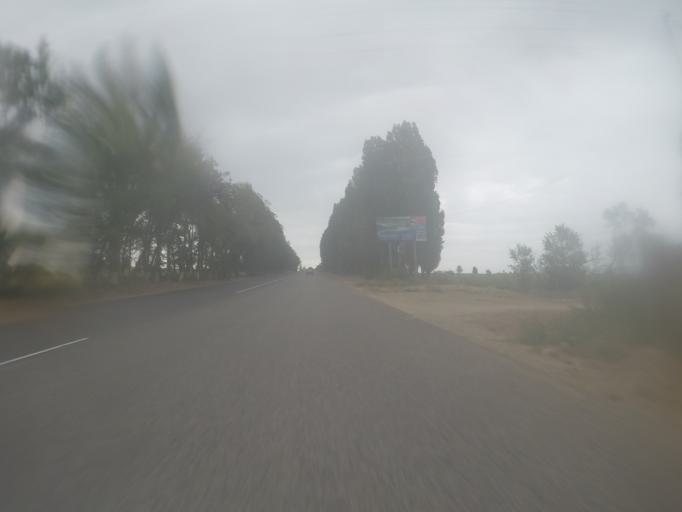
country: KG
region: Ysyk-Koel
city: Cholpon-Ata
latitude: 42.6691
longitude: 77.2805
